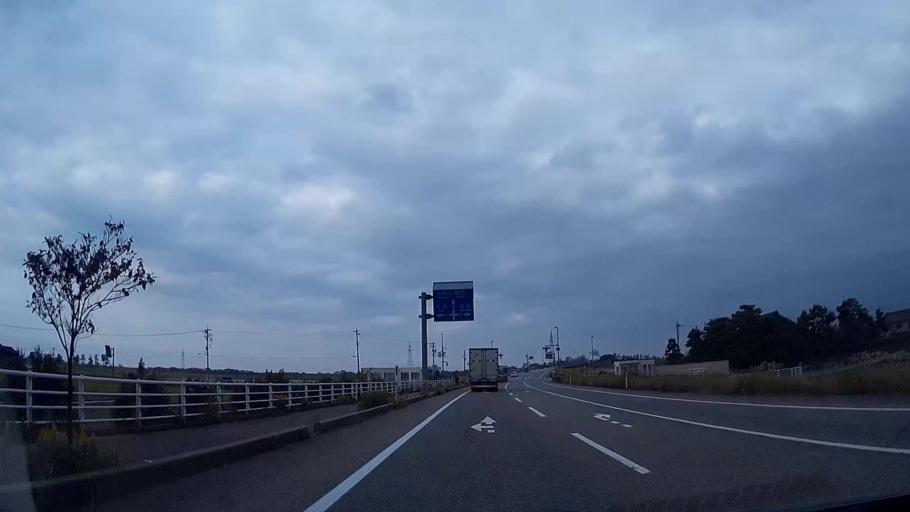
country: JP
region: Toyama
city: Nyuzen
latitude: 36.8982
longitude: 137.4451
